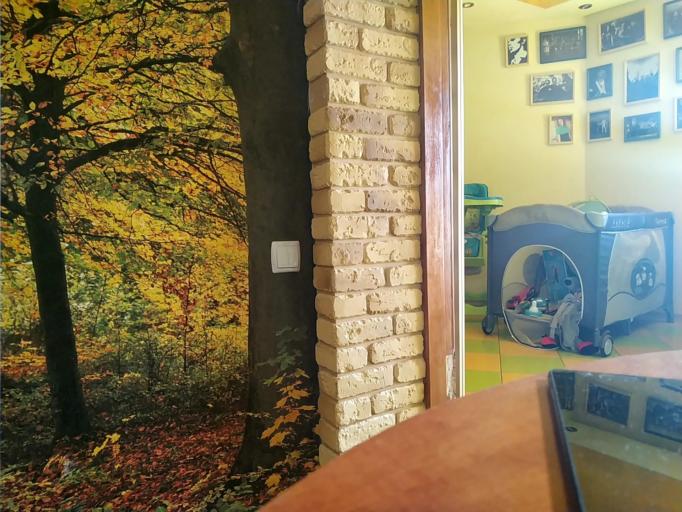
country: RU
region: Tverskaya
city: Vyshniy Volochek
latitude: 57.5433
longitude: 34.5958
